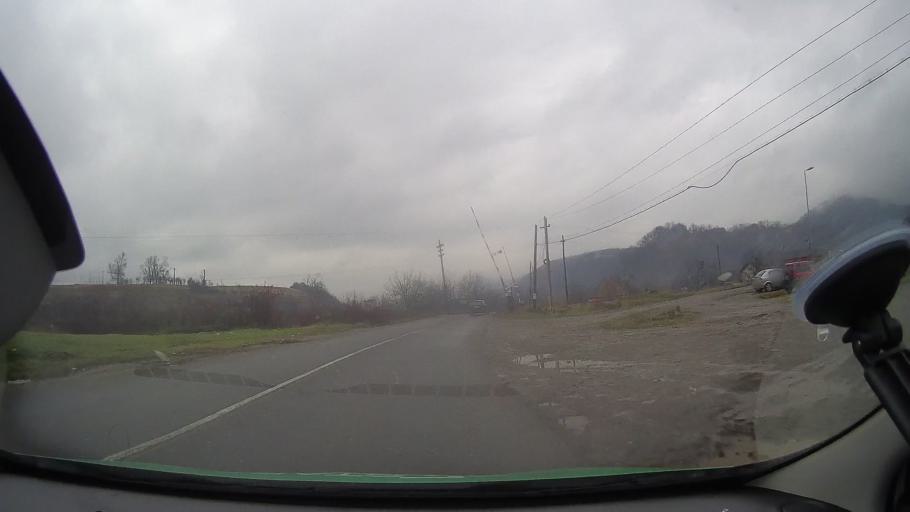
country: RO
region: Arad
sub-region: Comuna Gurahont
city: Gurahont
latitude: 46.2749
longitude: 22.3376
